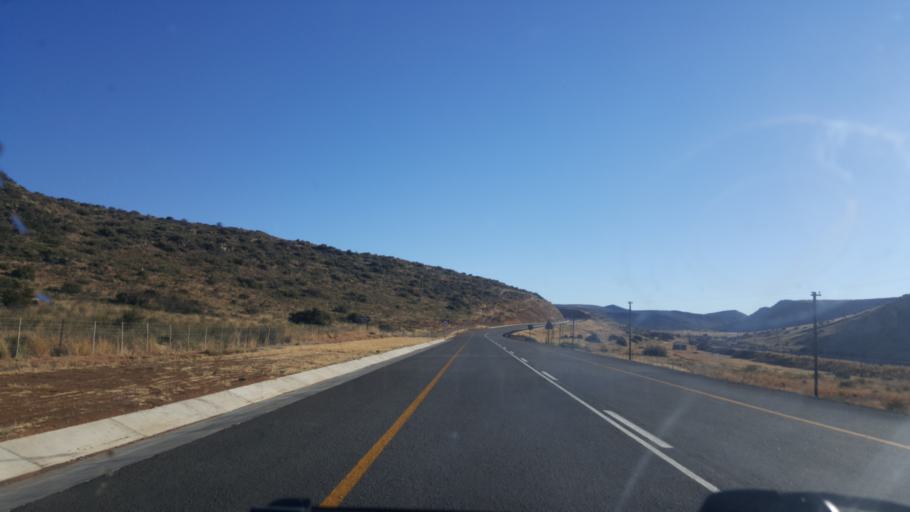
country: ZA
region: Eastern Cape
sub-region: Chris Hani District Municipality
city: Middelburg
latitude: -31.3850
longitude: 25.0318
